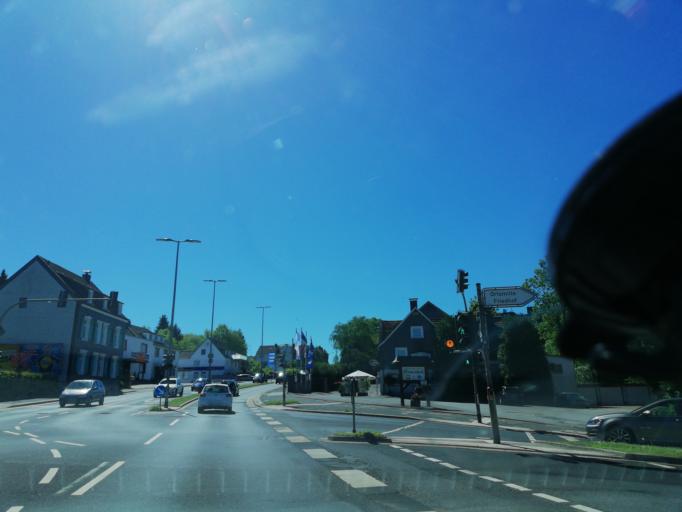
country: DE
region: North Rhine-Westphalia
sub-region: Regierungsbezirk Dusseldorf
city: Remscheid
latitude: 51.2069
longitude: 7.2445
